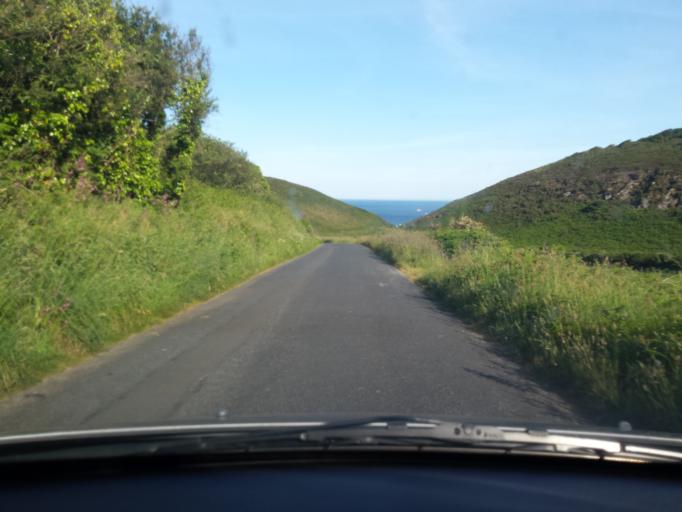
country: FR
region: Lower Normandy
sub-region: Departement de la Manche
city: Beaumont-Hague
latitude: 49.6880
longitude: -1.9286
